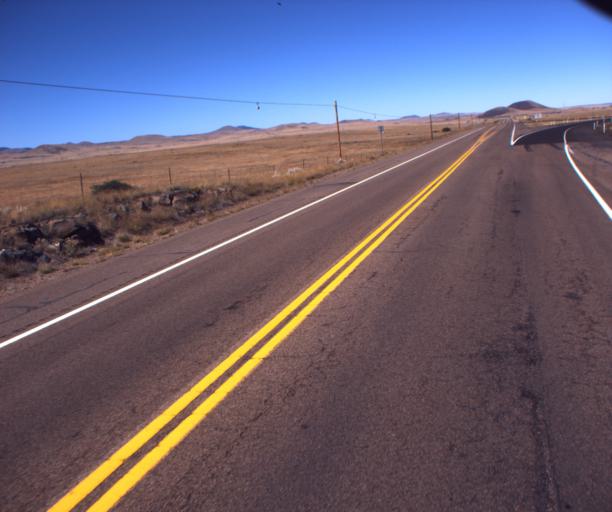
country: US
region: Arizona
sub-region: Apache County
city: Springerville
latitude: 34.1719
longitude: -109.3157
